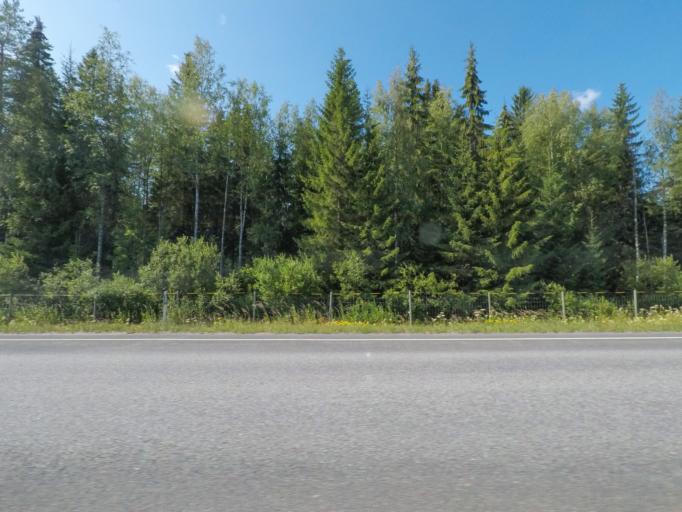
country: FI
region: Southern Savonia
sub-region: Pieksaemaeki
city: Juva
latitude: 61.8678
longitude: 27.7412
